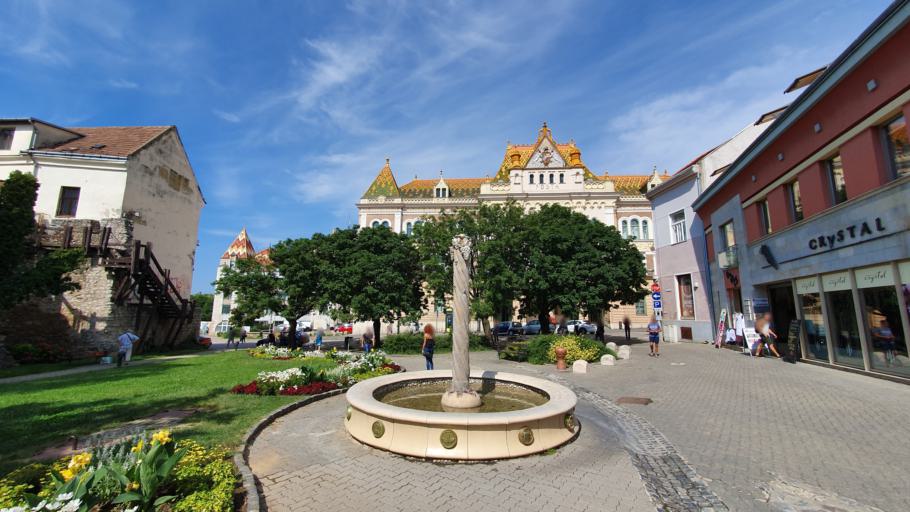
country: HU
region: Baranya
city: Pecs
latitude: 46.0734
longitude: 18.2274
